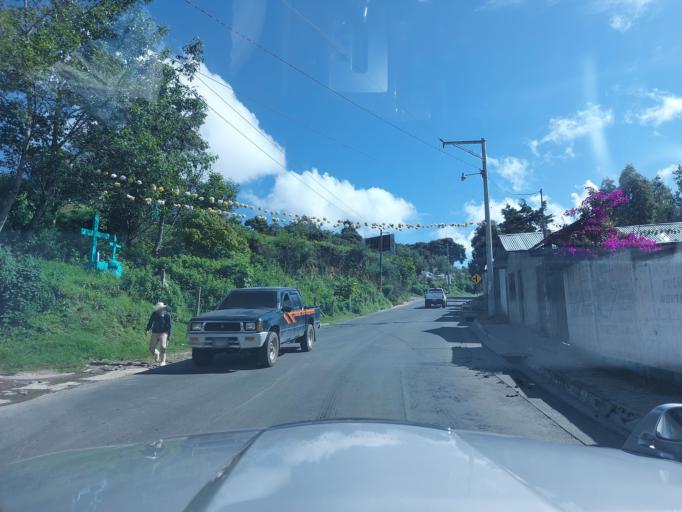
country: GT
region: Chimaltenango
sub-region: Municipio de Zaragoza
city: Zaragoza
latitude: 14.6454
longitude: -90.8982
